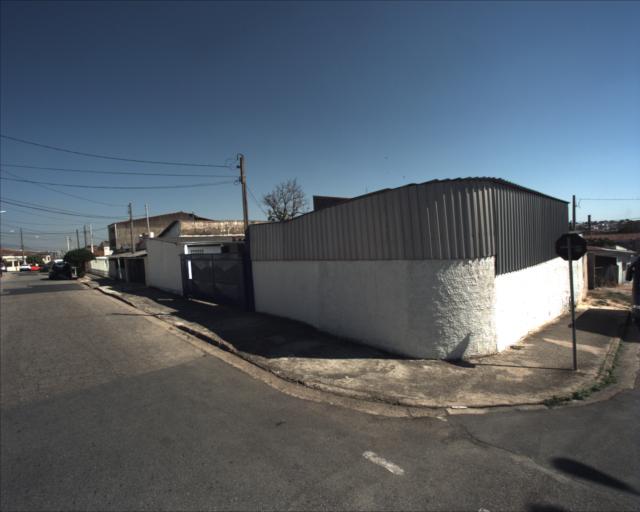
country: BR
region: Sao Paulo
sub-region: Sorocaba
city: Sorocaba
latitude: -23.4944
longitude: -47.4397
